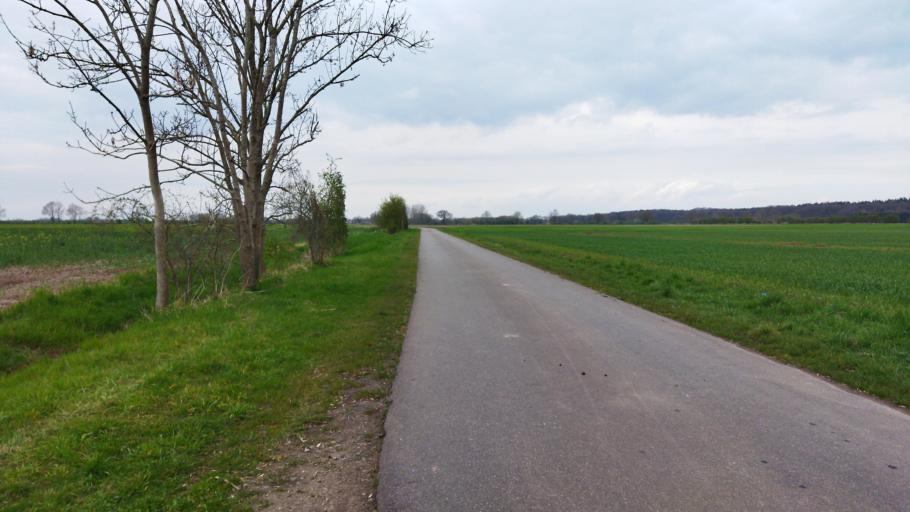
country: DE
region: Lower Saxony
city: Langwedel
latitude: 52.9721
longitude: 9.1597
